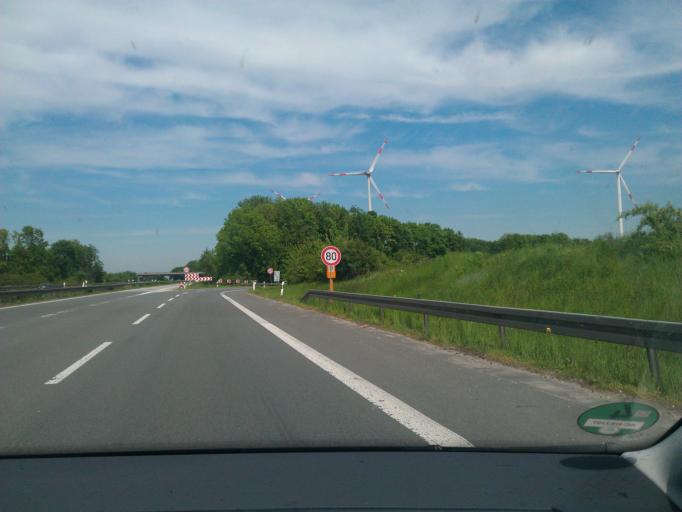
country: DE
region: North Rhine-Westphalia
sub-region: Regierungsbezirk Dusseldorf
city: Juchen
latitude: 51.0993
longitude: 6.4236
